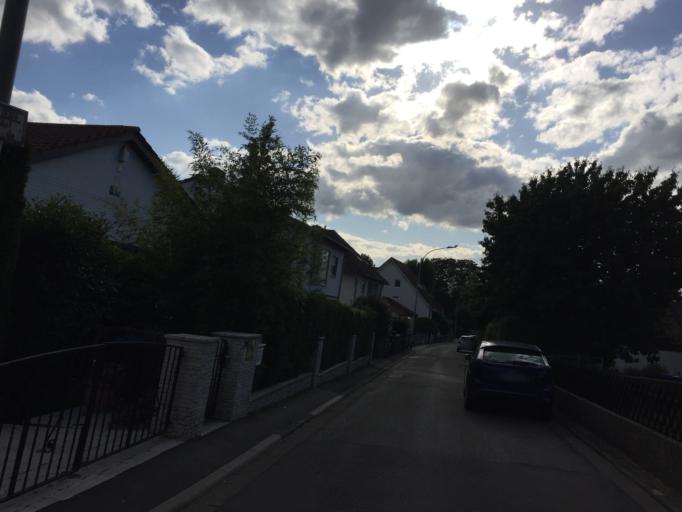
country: DE
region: Hesse
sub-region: Regierungsbezirk Darmstadt
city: Karben
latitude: 50.2308
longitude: 8.7751
